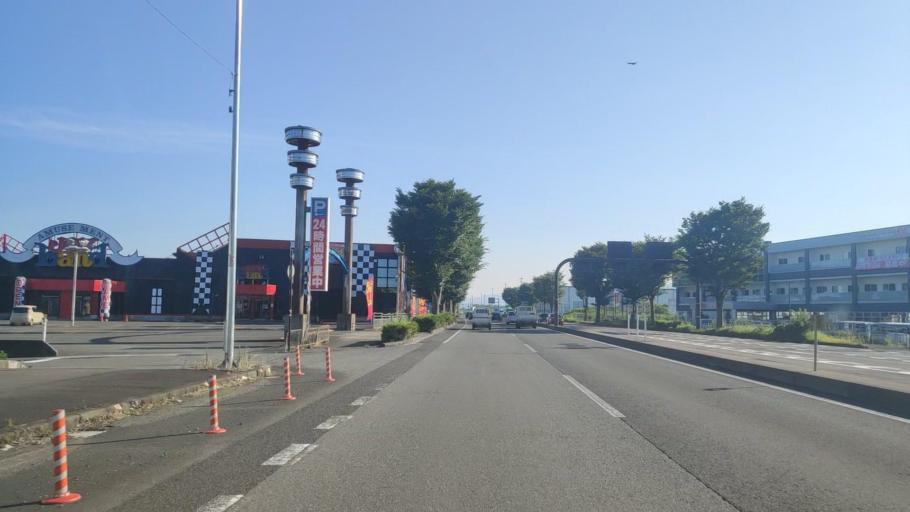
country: JP
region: Fukui
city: Fukui-shi
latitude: 36.0983
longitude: 136.2527
